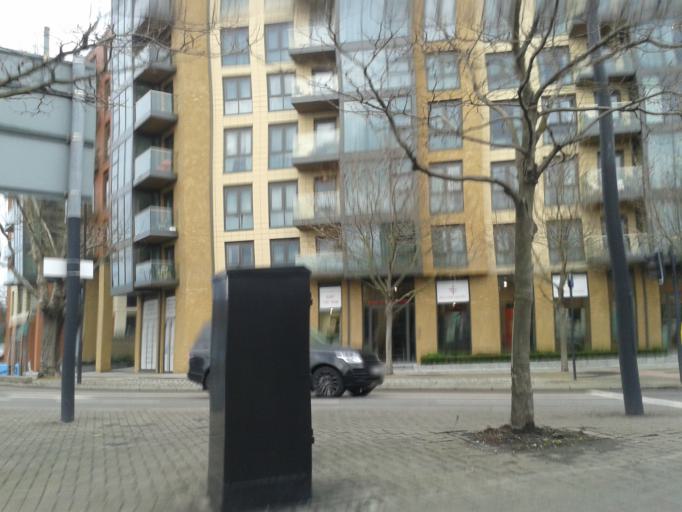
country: GB
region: England
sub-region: Greater London
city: Earlsfield
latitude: 51.4628
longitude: -0.1846
